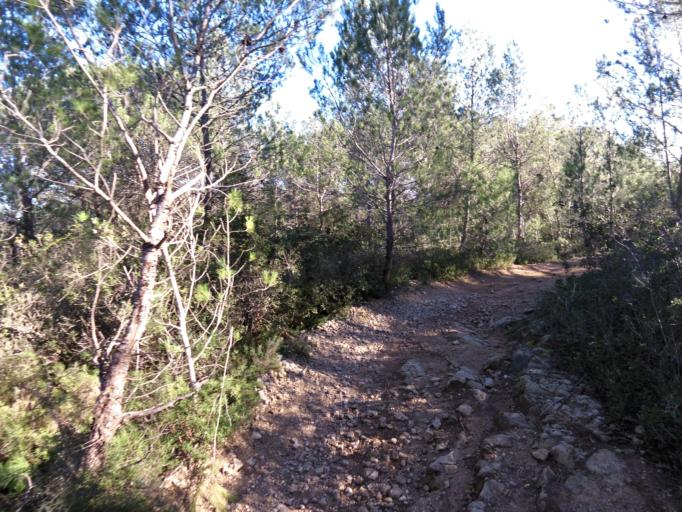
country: FR
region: Languedoc-Roussillon
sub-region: Departement de l'Herault
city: Villetelle
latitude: 43.7361
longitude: 4.1555
